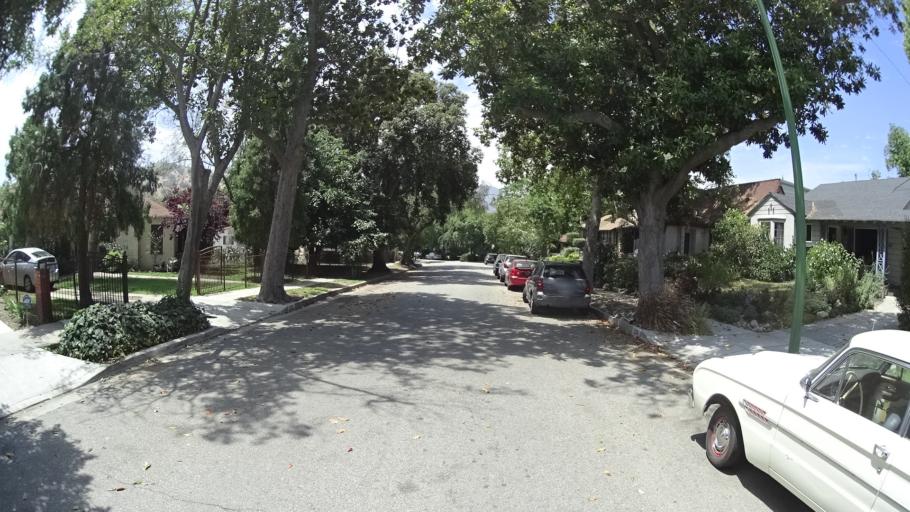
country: US
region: California
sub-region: Los Angeles County
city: Burbank
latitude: 34.1599
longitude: -118.3000
